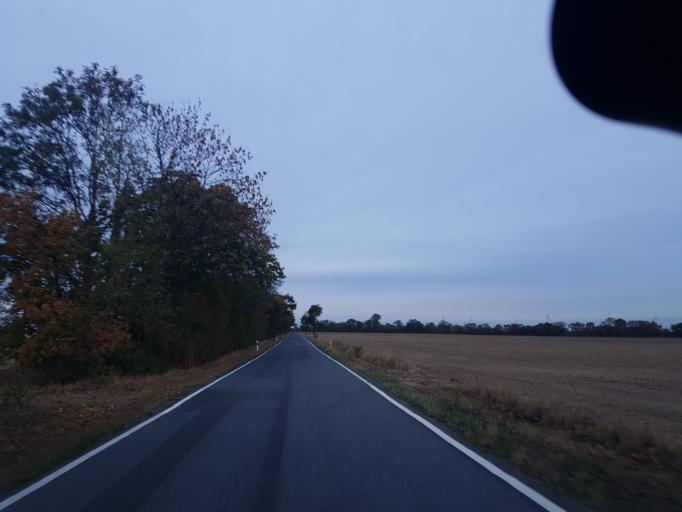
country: DE
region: Brandenburg
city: Muhlberg
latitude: 51.4981
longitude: 13.2492
